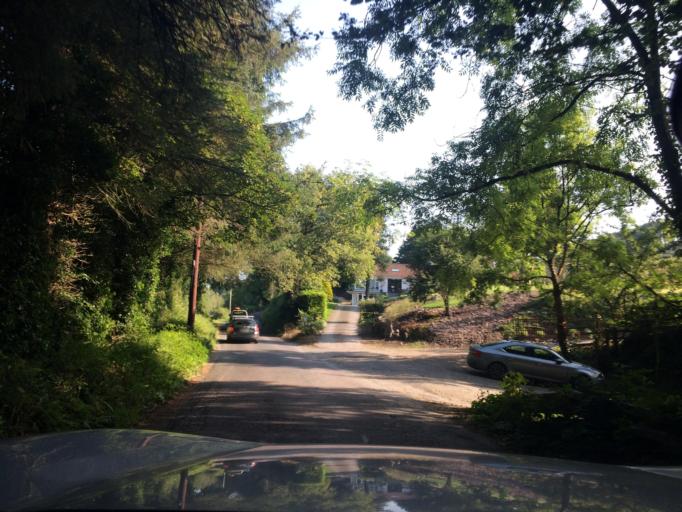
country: IE
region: Munster
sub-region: Waterford
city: Dungarvan
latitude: 52.1337
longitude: -7.6789
